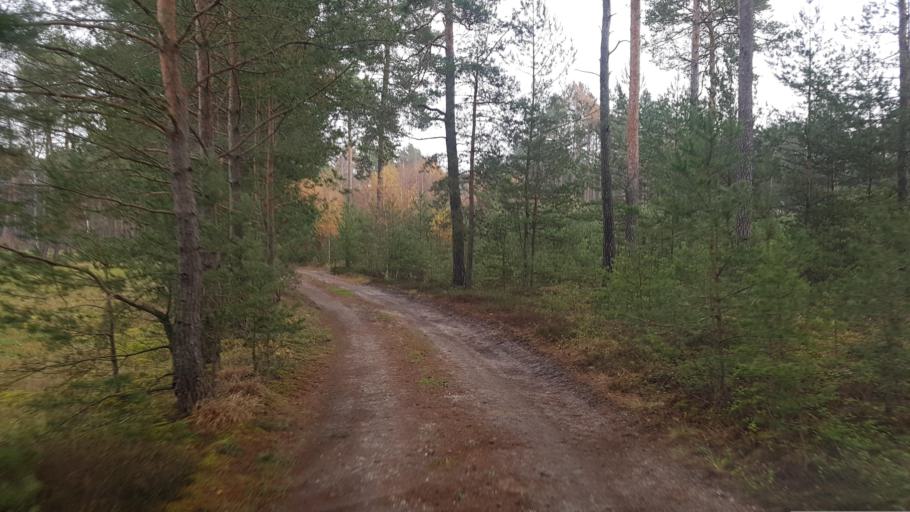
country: DE
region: Brandenburg
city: Sallgast
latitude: 51.6477
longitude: 13.8345
